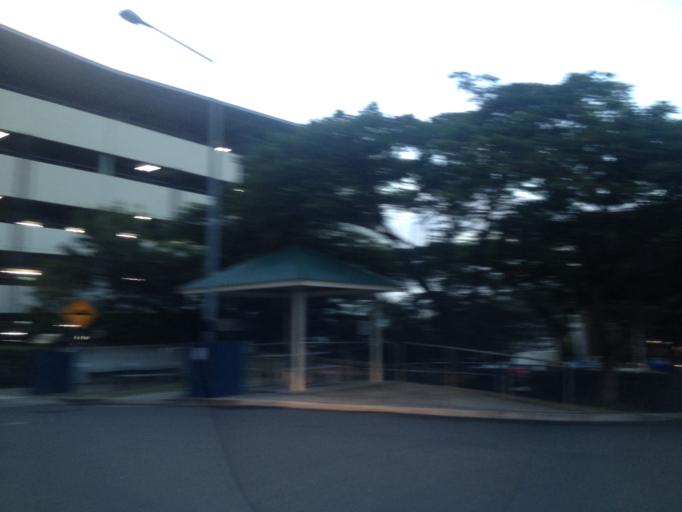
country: AU
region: Queensland
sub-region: Brisbane
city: Windsor
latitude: -27.4463
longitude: 153.0286
